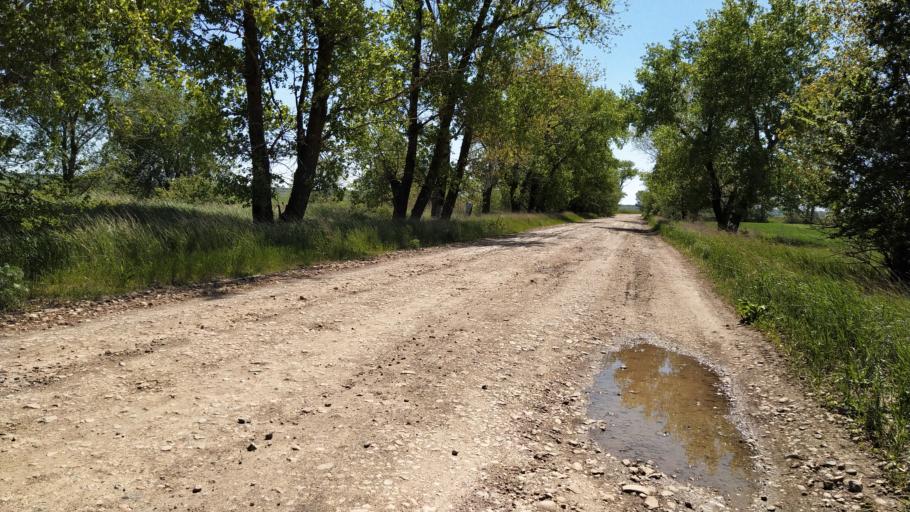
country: RU
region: Rostov
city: Kuleshovka
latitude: 47.0591
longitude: 39.6250
